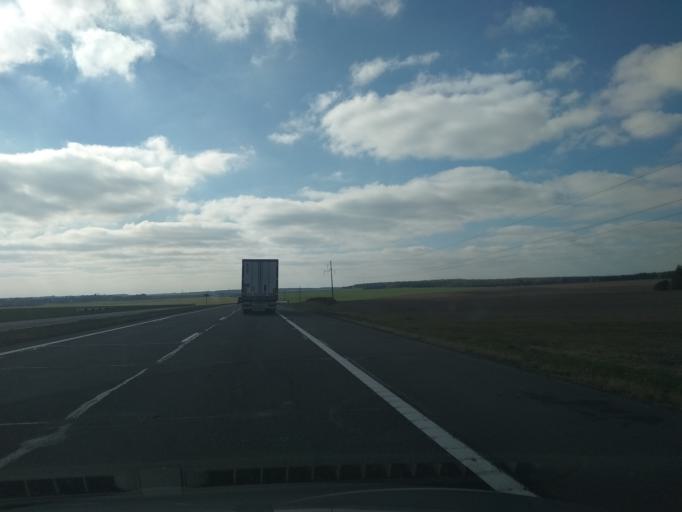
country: BY
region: Minsk
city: Novy Svyerzhan'
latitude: 53.4640
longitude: 26.6113
